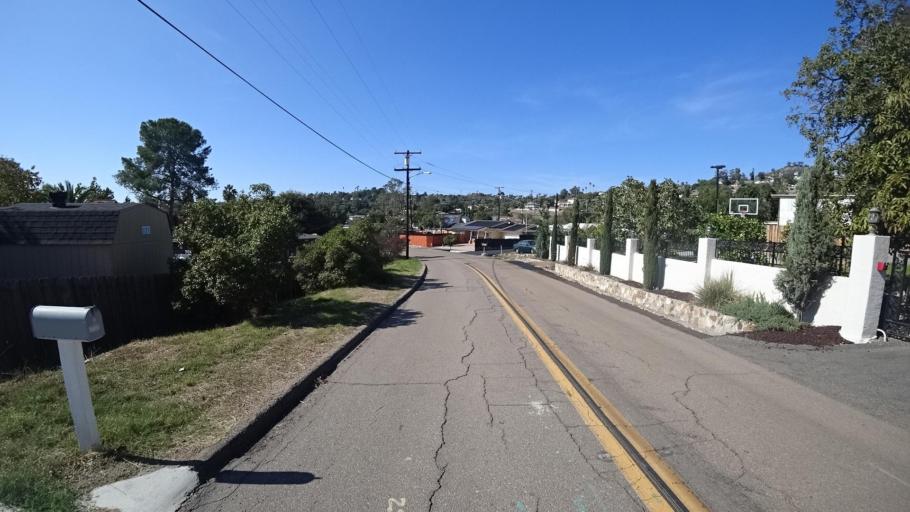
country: US
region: California
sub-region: San Diego County
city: Spring Valley
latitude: 32.7513
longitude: -116.9825
